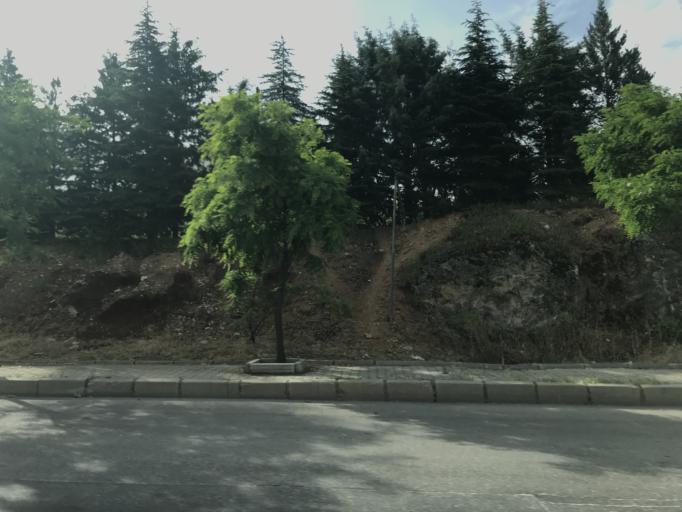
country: TR
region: Gaziantep
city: Sehitkamil
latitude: 37.1589
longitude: 37.2875
